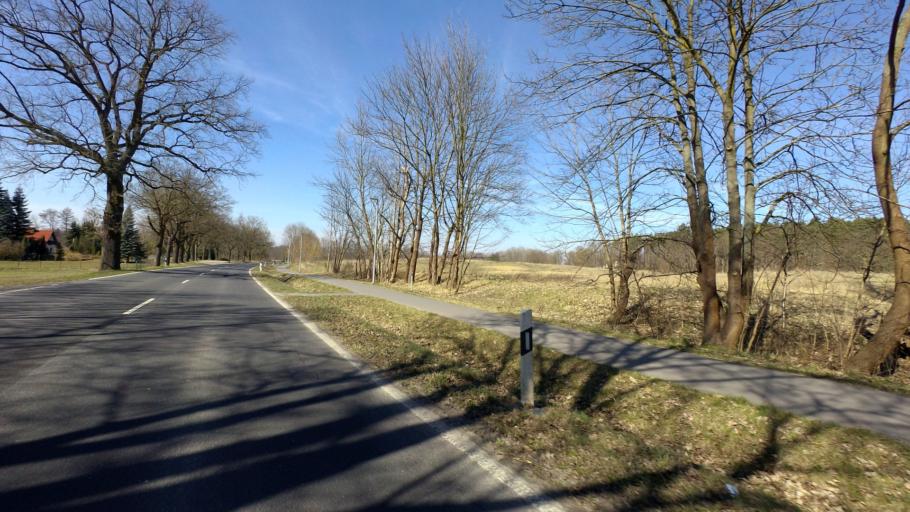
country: DE
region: Brandenburg
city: Muncheberg
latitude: 52.5180
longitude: 14.1101
